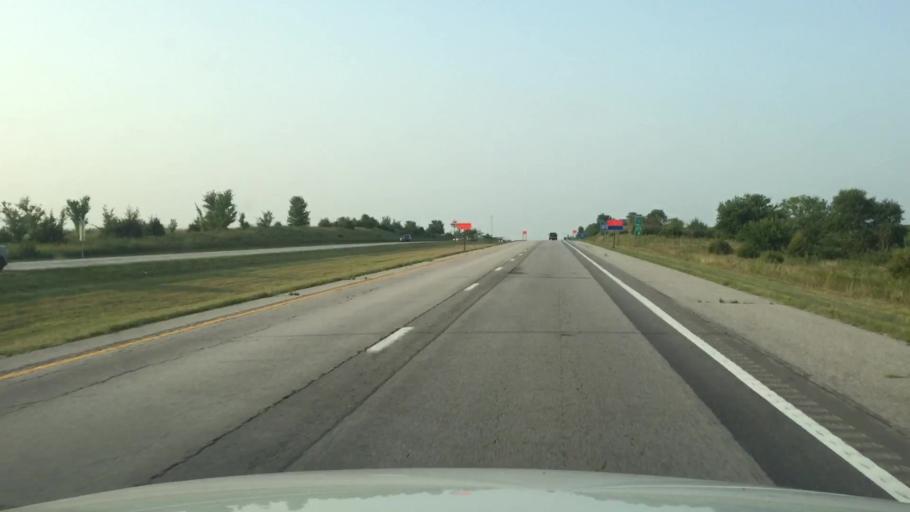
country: US
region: Iowa
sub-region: Decatur County
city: Lamoni
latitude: 40.4533
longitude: -93.9805
